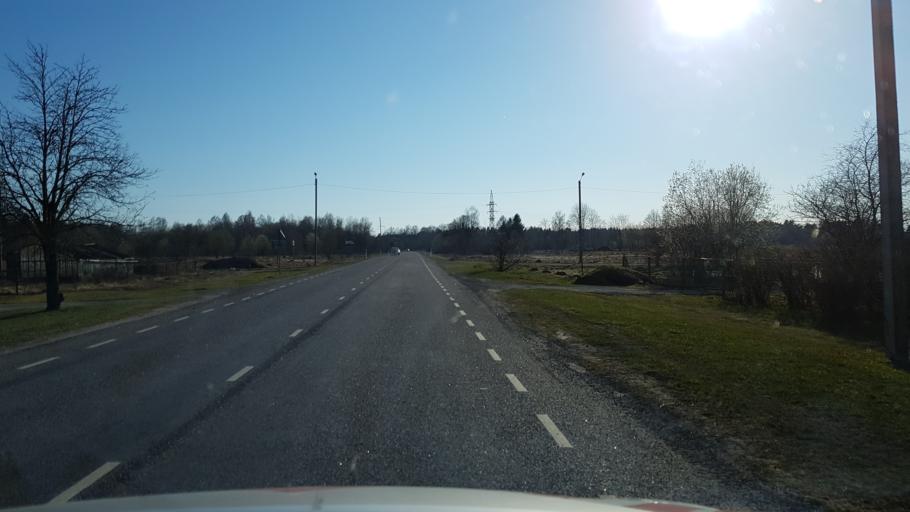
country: EE
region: Ida-Virumaa
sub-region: Kohtla-Jaerve linn
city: Kohtla-Jarve
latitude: 59.3355
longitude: 27.2858
